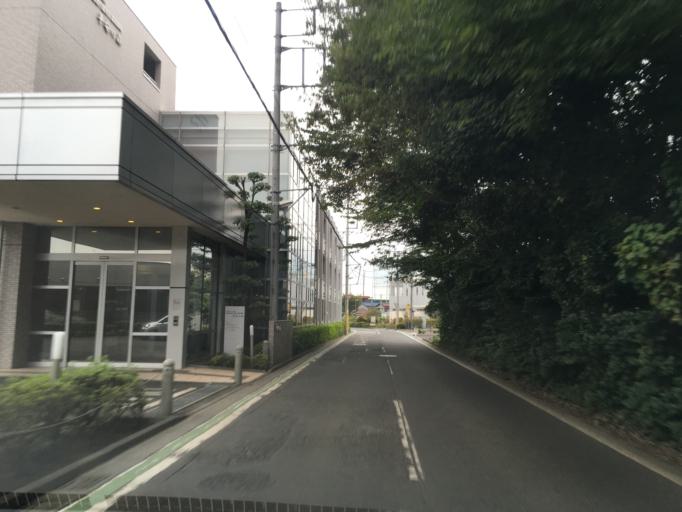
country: JP
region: Saitama
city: Tokorozawa
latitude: 35.8079
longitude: 139.4268
